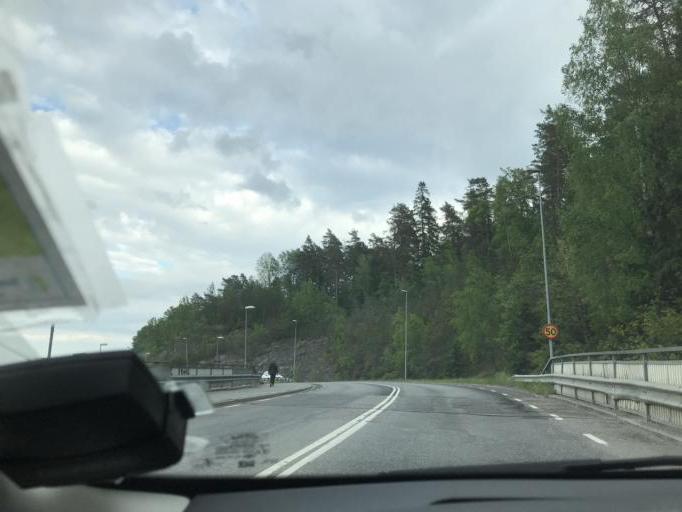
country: SE
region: Stockholm
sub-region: Botkyrka Kommun
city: Tumba
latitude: 59.2001
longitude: 17.8146
